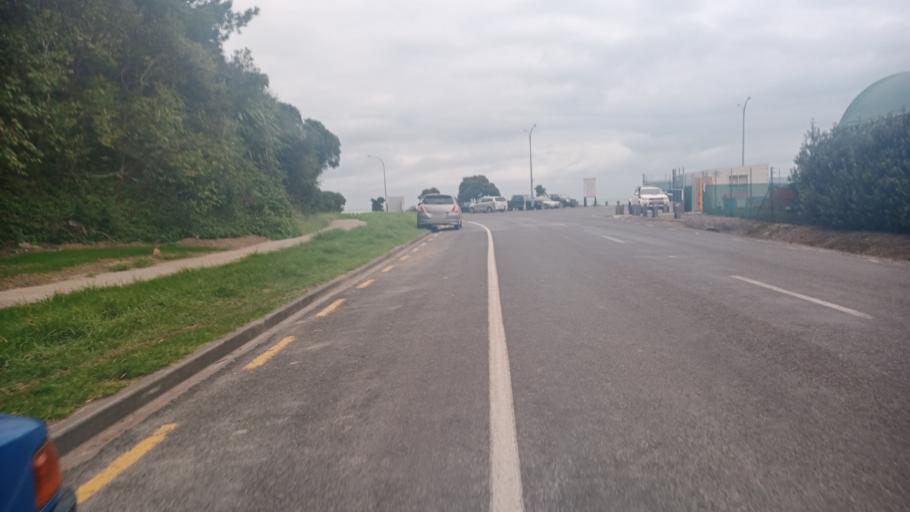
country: NZ
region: Gisborne
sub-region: Gisborne District
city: Gisborne
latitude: -38.6793
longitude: 178.0271
